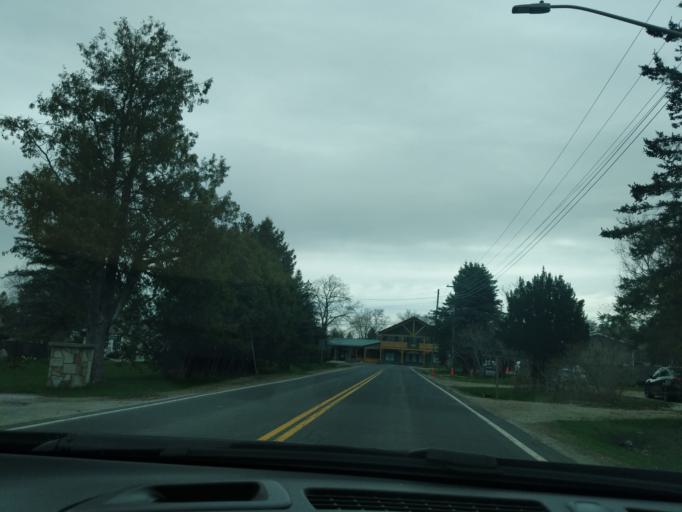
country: CA
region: Ontario
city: Orangeville
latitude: 44.0214
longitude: -79.9702
